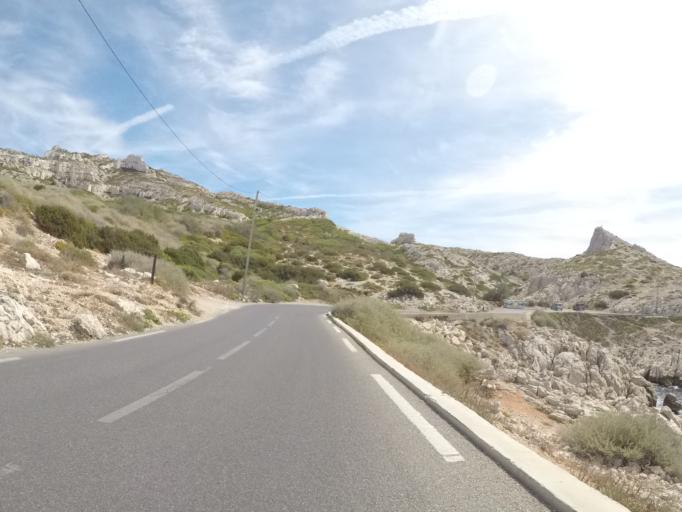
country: FR
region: Provence-Alpes-Cote d'Azur
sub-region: Departement des Bouches-du-Rhone
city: Marseille 08
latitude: 43.2208
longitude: 5.3458
